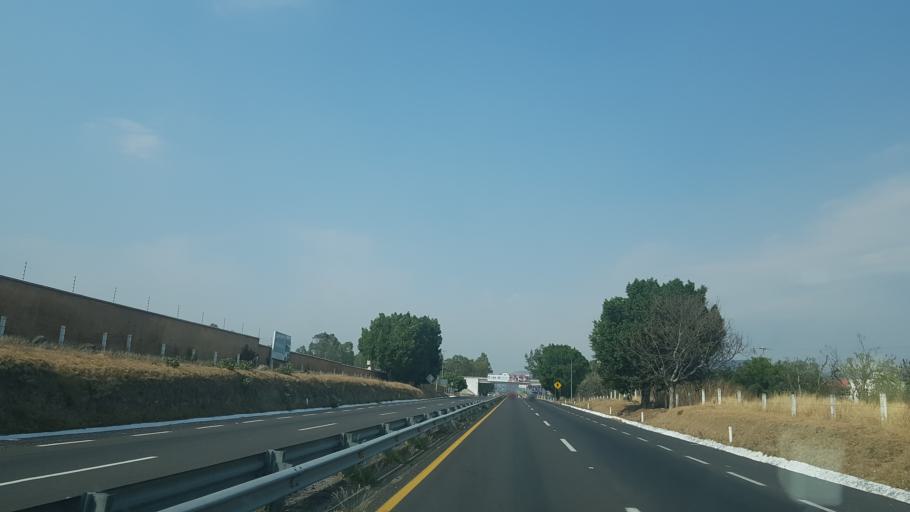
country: MX
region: Puebla
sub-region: Atlixco
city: San Agustin Huixaxtla
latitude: 18.9263
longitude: -98.3993
